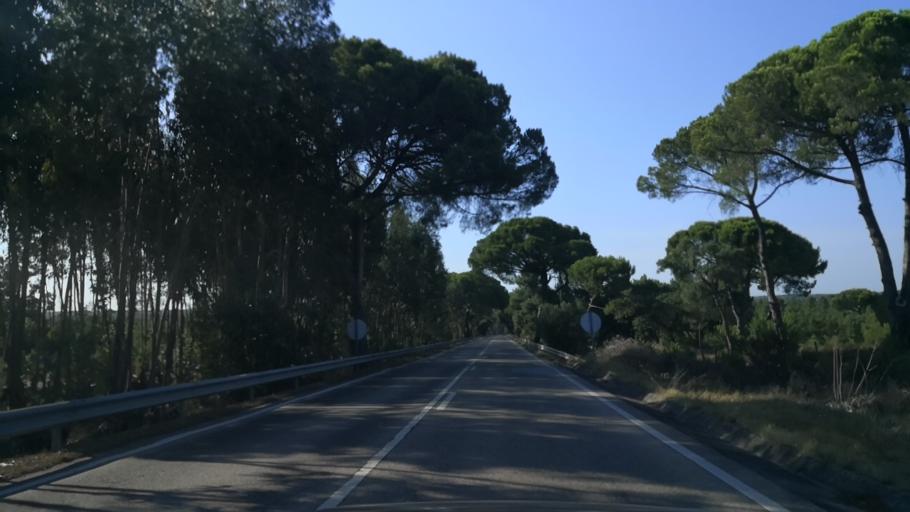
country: PT
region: Santarem
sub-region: Coruche
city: Coruche
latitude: 38.9846
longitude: -8.5488
